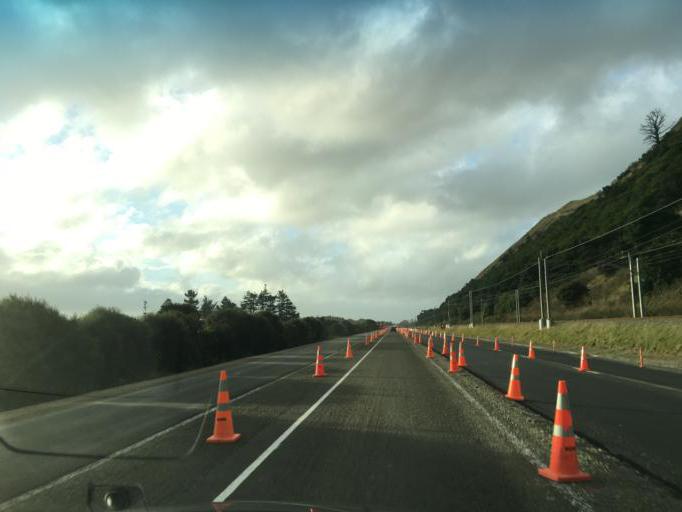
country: NZ
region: Wellington
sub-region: Kapiti Coast District
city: Paraparaumu
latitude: -40.9510
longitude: 174.9893
